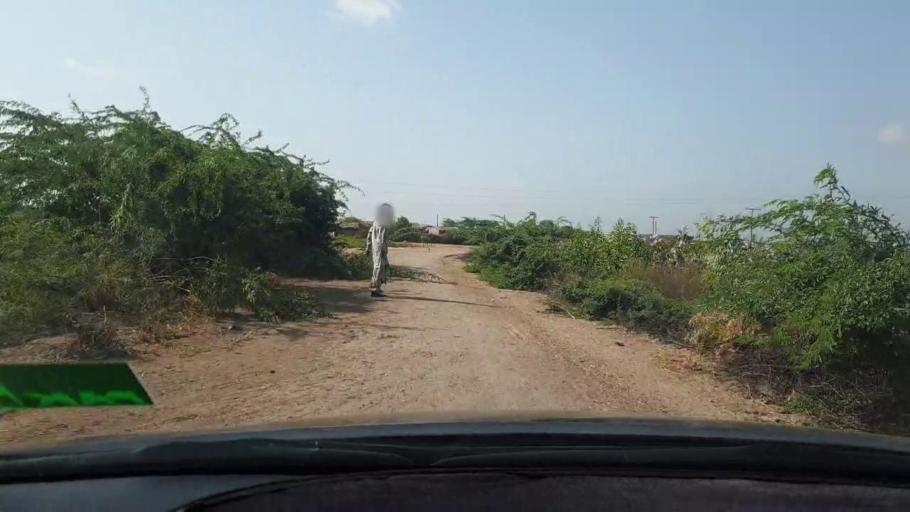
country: PK
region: Sindh
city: Tando Bago
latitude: 24.8625
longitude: 68.9938
